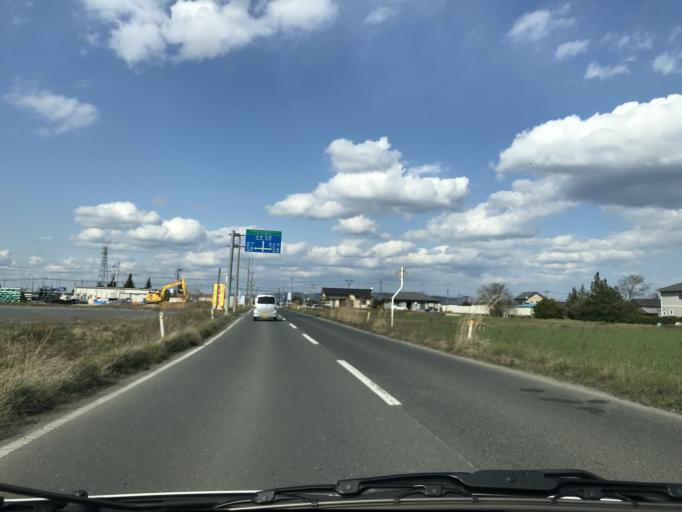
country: JP
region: Miyagi
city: Wakuya
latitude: 38.6953
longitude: 141.2340
